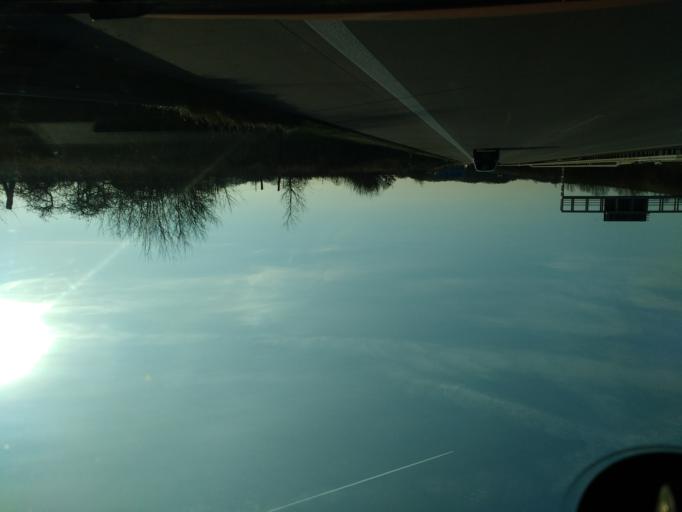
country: DE
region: Brandenburg
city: Ahrensfelde
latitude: 52.6055
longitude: 13.5980
